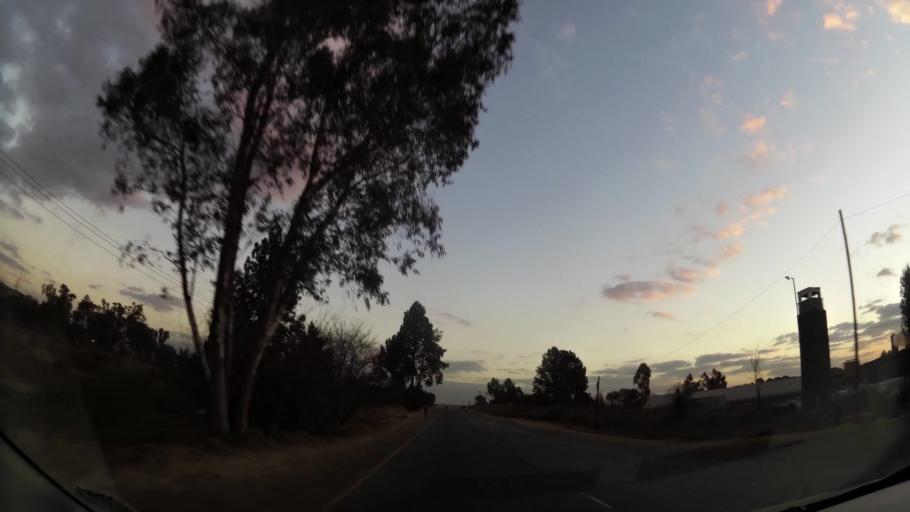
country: ZA
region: Gauteng
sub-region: West Rand District Municipality
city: Krugersdorp
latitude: -26.0406
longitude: 27.7205
